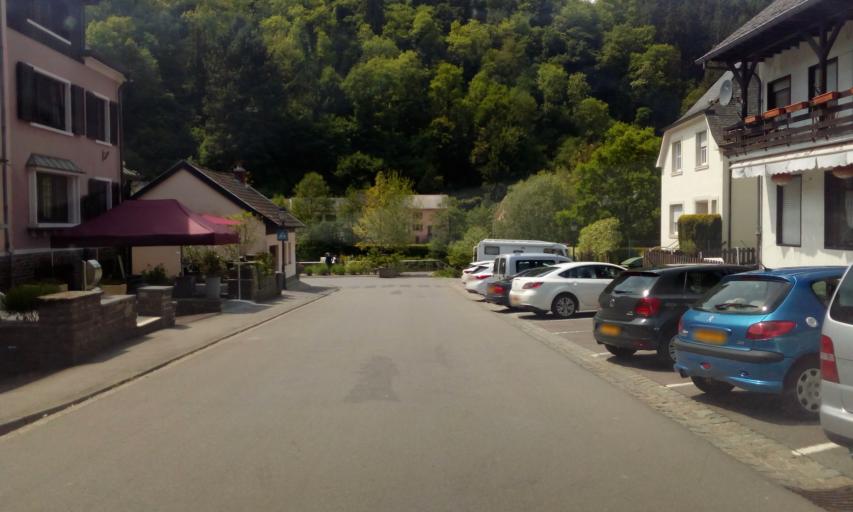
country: LU
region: Diekirch
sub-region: Canton de Vianden
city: Vianden
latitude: 49.9358
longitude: 6.2064
